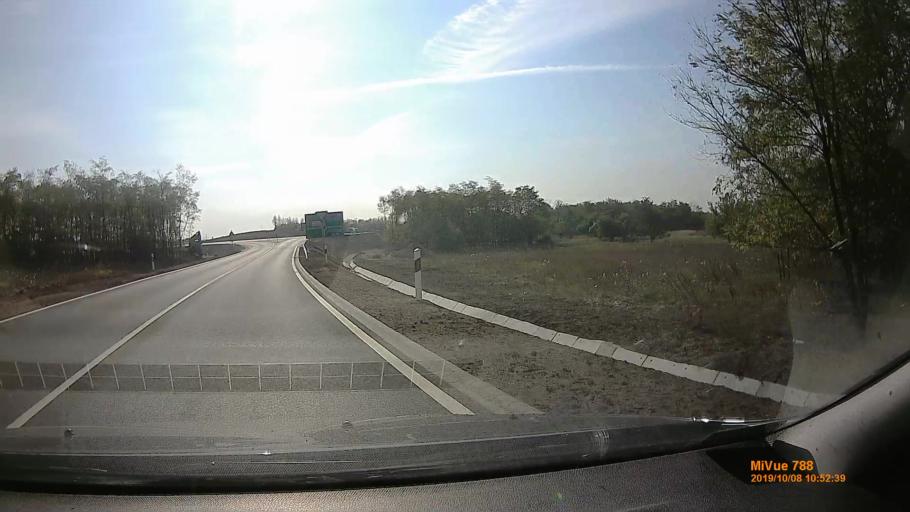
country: HU
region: Pest
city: Dunakeszi
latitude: 47.6565
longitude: 19.1562
